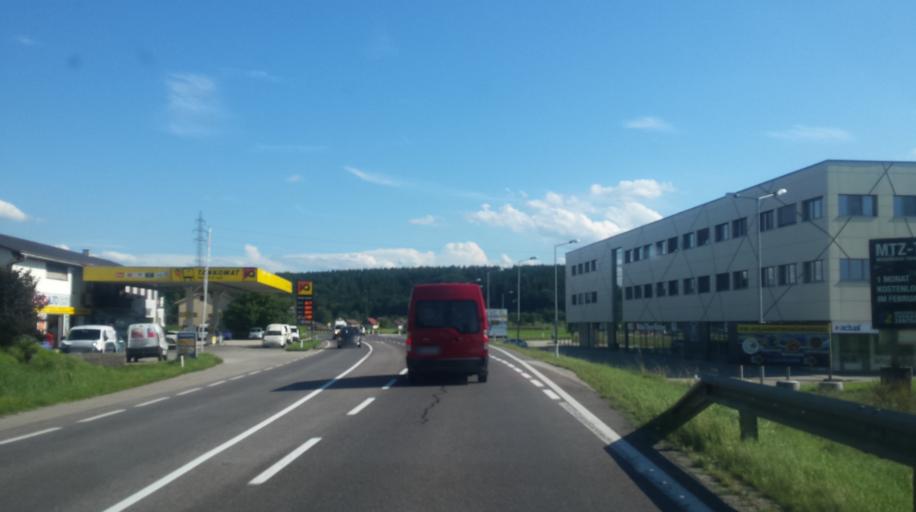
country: AT
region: Upper Austria
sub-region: Politischer Bezirk Vocklabruck
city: Attnang-Puchheim
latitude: 47.9916
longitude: 13.6841
